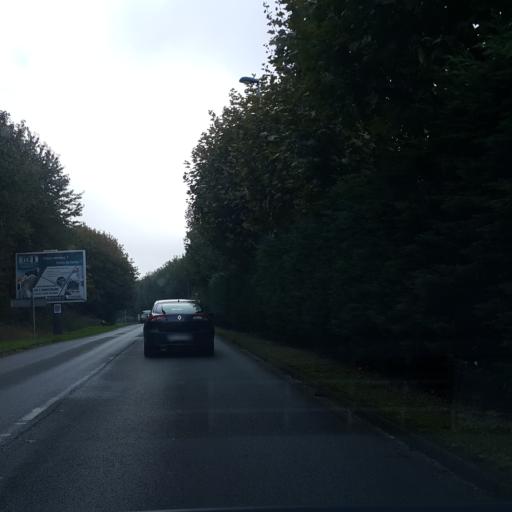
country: FR
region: Ile-de-France
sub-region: Departement de l'Essonne
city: Saint-Pierre-du-Perray
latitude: 48.6168
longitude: 2.5002
